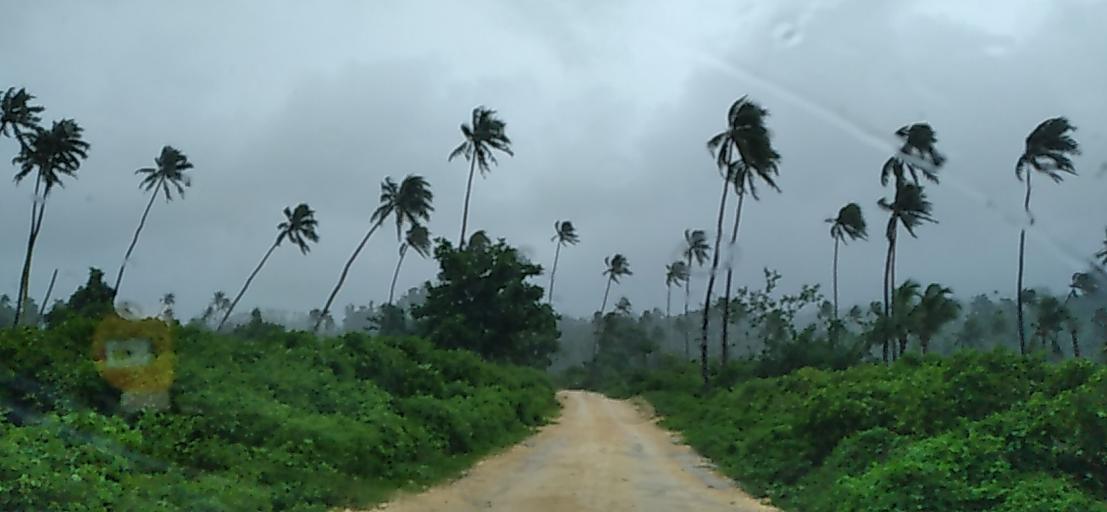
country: VU
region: Penama
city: Saratamata
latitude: -15.9569
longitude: 168.1956
